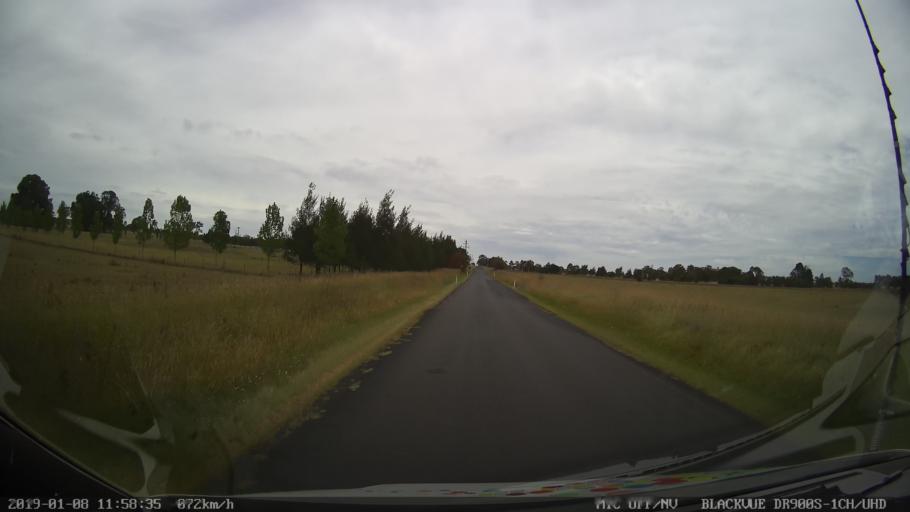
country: AU
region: New South Wales
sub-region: Armidale Dumaresq
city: Armidale
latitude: -30.4570
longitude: 151.5772
